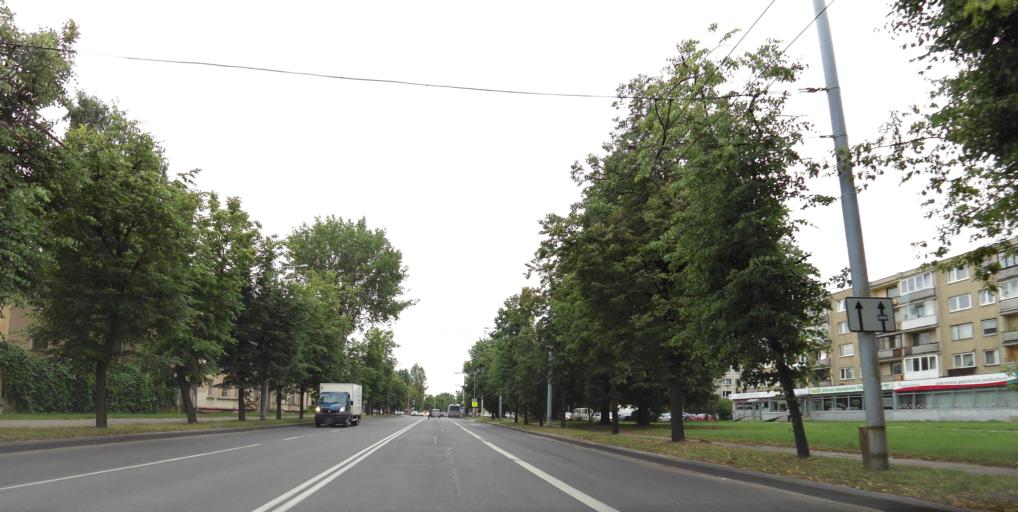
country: LT
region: Vilnius County
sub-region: Vilnius
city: Vilnius
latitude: 54.7102
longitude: 25.2861
